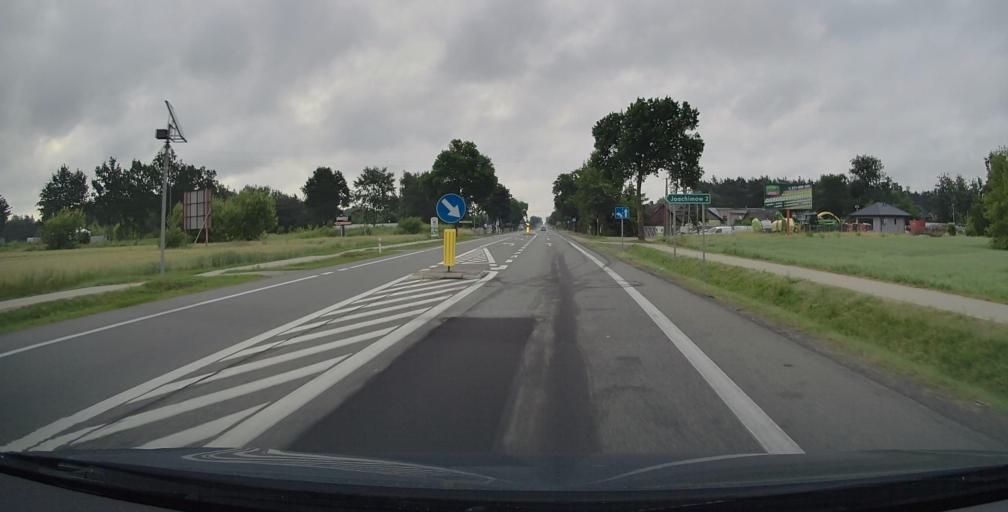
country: PL
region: Masovian Voivodeship
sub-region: Siedlce
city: Siedlce
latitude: 52.1250
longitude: 22.3463
